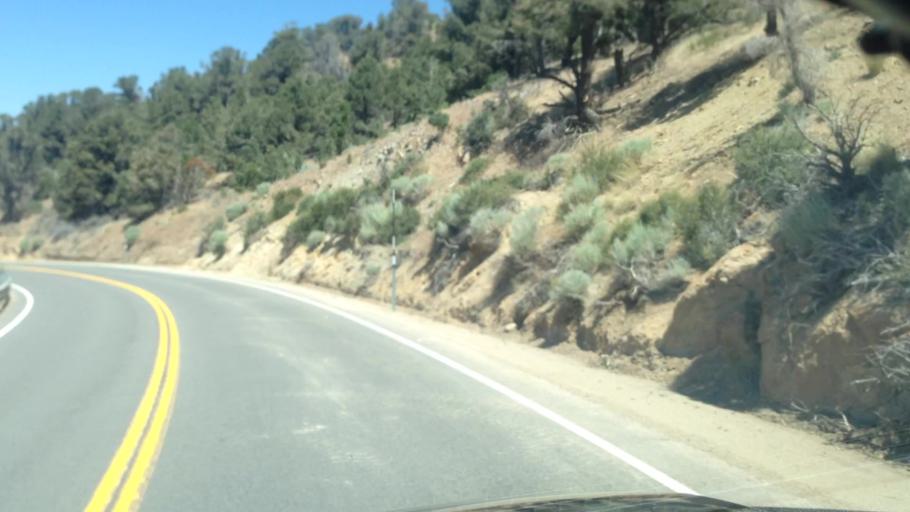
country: US
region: Nevada
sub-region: Storey County
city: Virginia City
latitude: 39.3572
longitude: -119.6622
